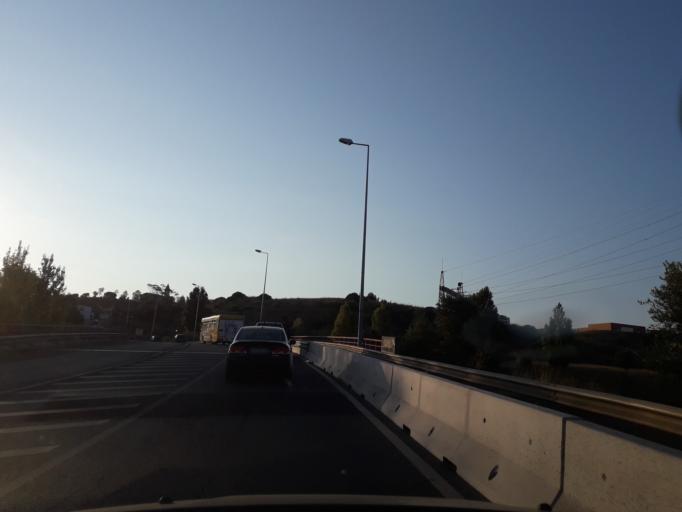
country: PT
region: Lisbon
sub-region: Odivelas
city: Pontinha
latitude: 38.7724
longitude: -9.2036
